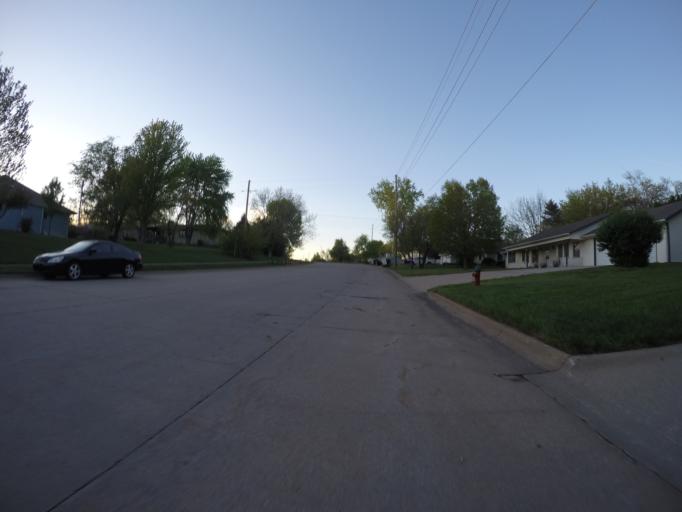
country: US
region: Kansas
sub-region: Riley County
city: Manhattan
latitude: 39.1608
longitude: -96.6113
